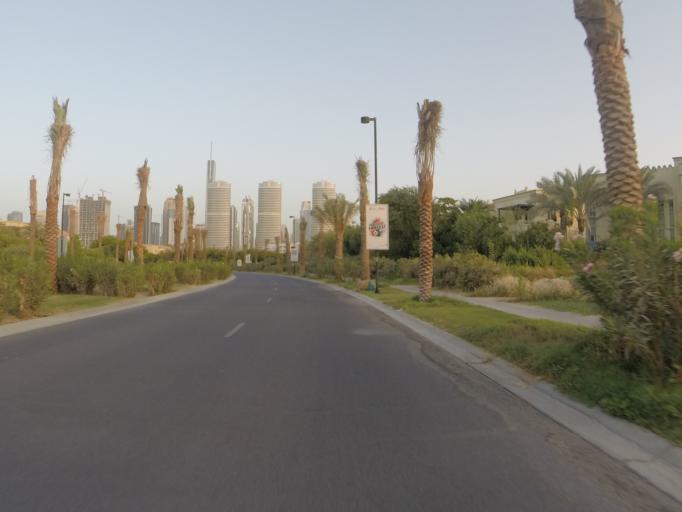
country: AE
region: Dubai
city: Dubai
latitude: 25.0632
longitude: 55.1531
